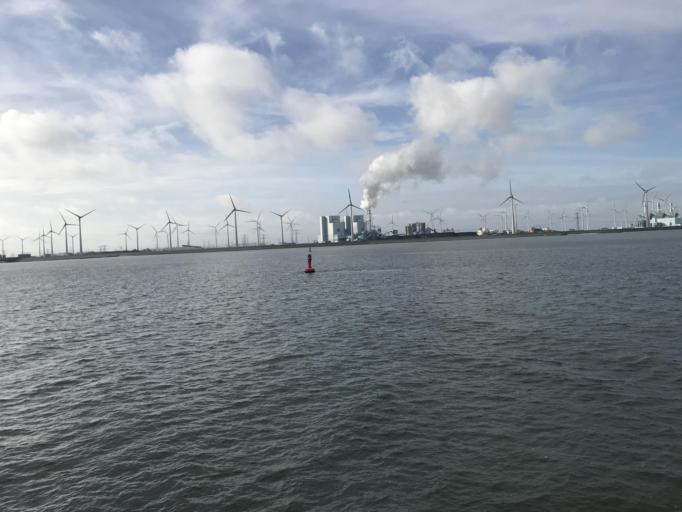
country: NL
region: Groningen
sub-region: Gemeente Delfzijl
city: Delfzijl
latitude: 53.4542
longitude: 6.8860
